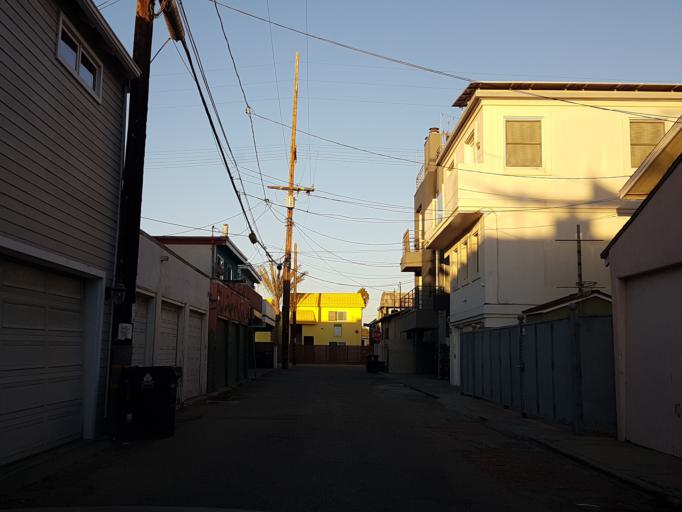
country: US
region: California
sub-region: Los Angeles County
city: Marina del Rey
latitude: 33.9823
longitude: -118.4687
